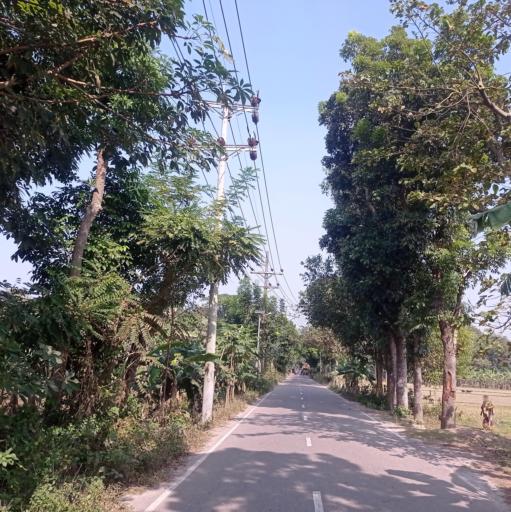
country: BD
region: Dhaka
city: Narsingdi
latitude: 24.0365
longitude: 90.6760
